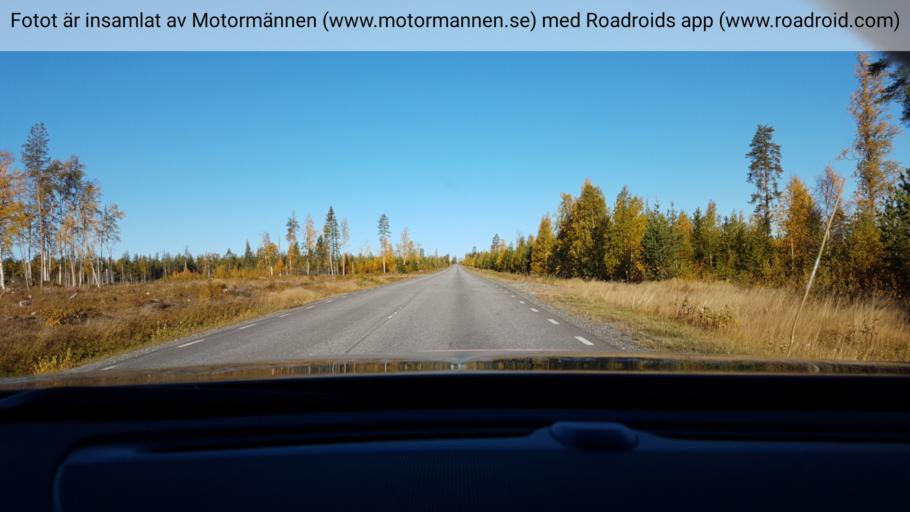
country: SE
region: Vaesterbotten
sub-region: Skelleftea Kommun
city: Storvik
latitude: 65.3424
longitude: 20.5155
